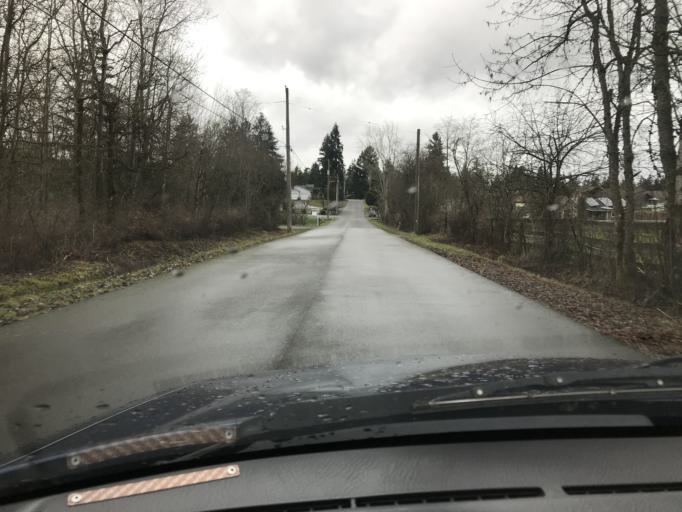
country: US
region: Washington
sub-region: Pierce County
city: Waller
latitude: 47.1883
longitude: -122.3699
